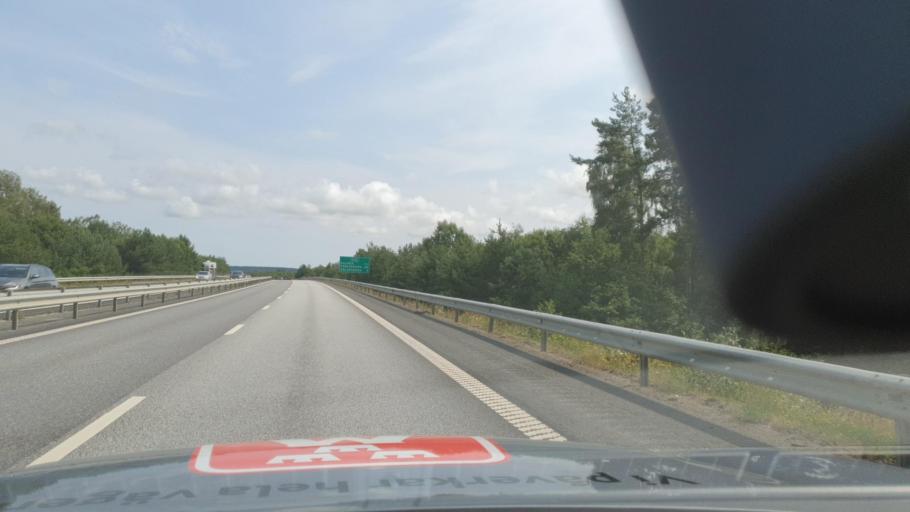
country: SE
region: Skane
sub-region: Bromolla Kommun
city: Bromoella
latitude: 56.0642
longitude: 14.5099
